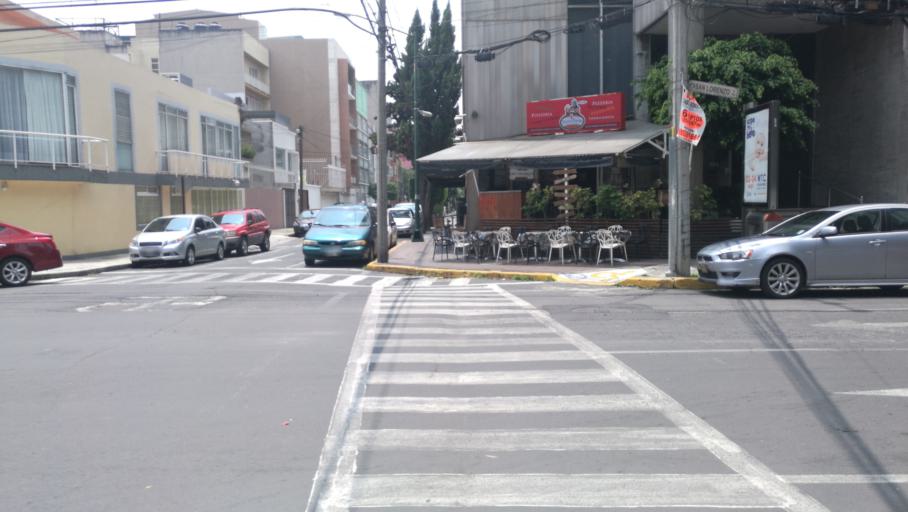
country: MX
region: Mexico City
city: Colonia del Valle
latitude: 19.3751
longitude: -99.1763
